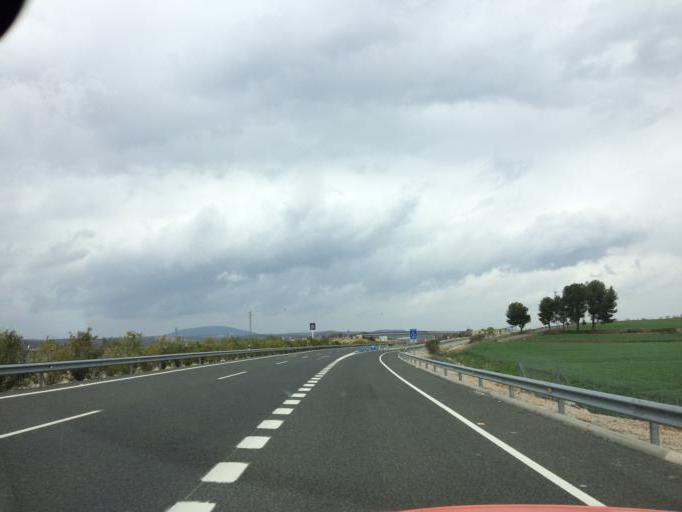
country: ES
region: Andalusia
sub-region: Provincia de Malaga
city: Antequera
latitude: 37.1082
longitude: -4.5616
